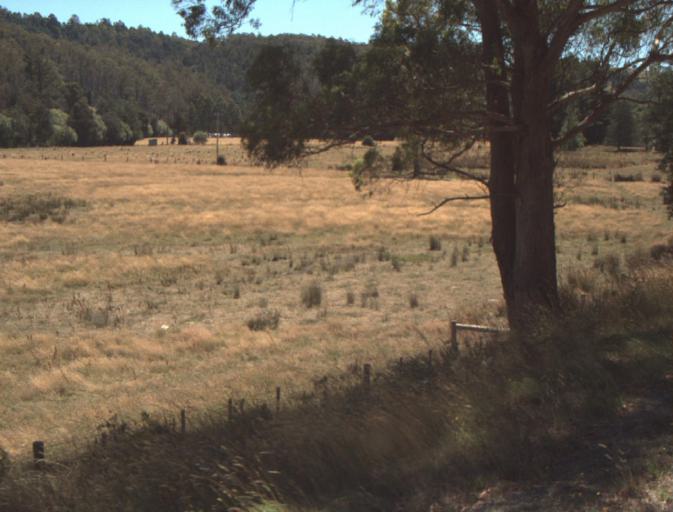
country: AU
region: Tasmania
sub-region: Dorset
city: Scottsdale
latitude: -41.3172
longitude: 147.3660
